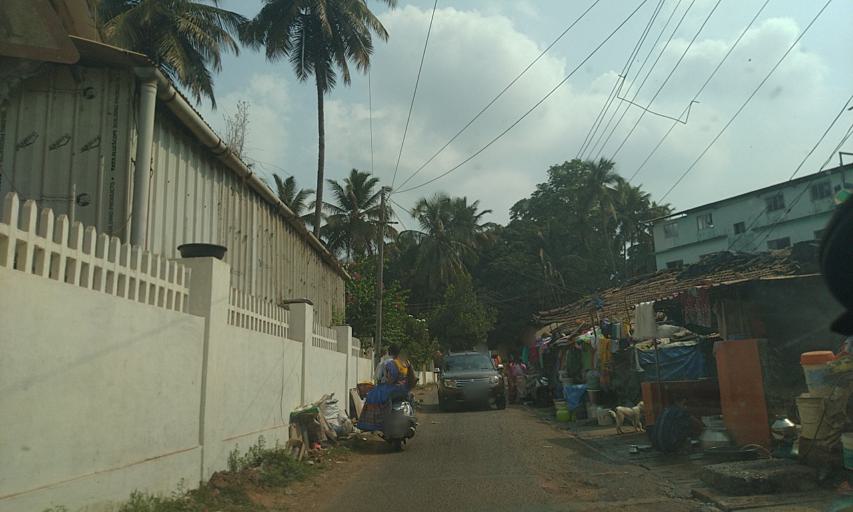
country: IN
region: Goa
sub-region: North Goa
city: Taleigao
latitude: 15.4754
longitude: 73.8436
